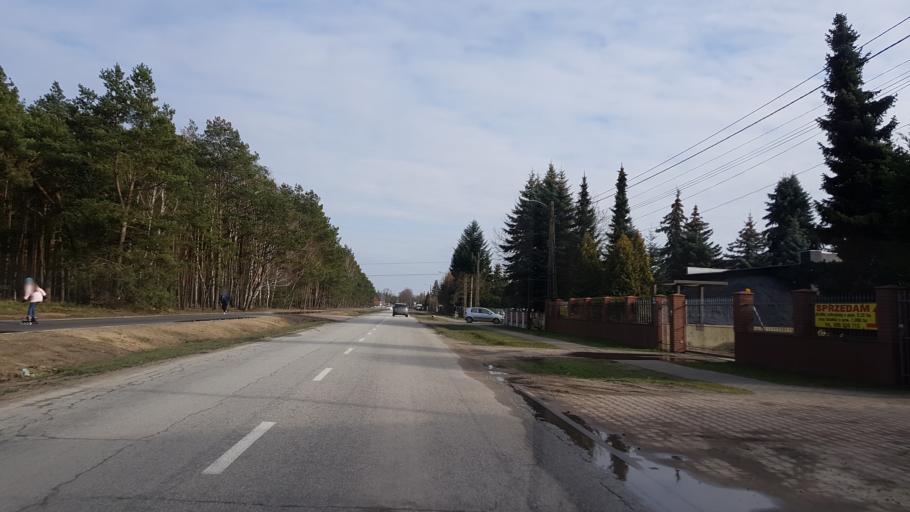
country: PL
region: West Pomeranian Voivodeship
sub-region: Powiat policki
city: Dobra
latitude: 53.4780
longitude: 14.4286
